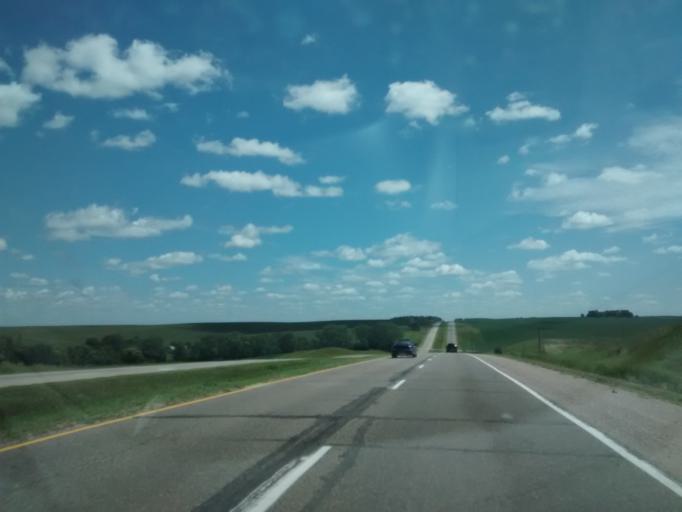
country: US
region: Iowa
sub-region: Woodbury County
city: Moville
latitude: 42.4749
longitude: -96.1620
